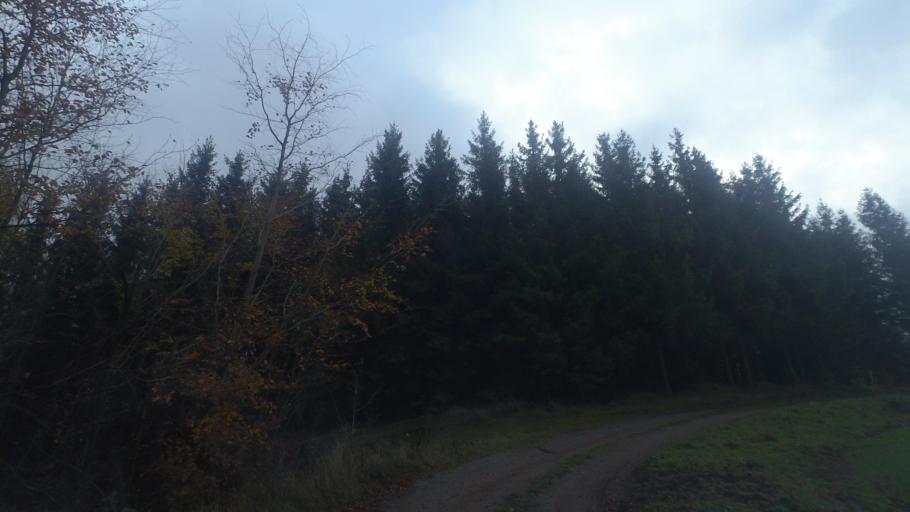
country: DE
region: Thuringia
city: Eisfeld
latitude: 50.4844
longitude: 10.8656
